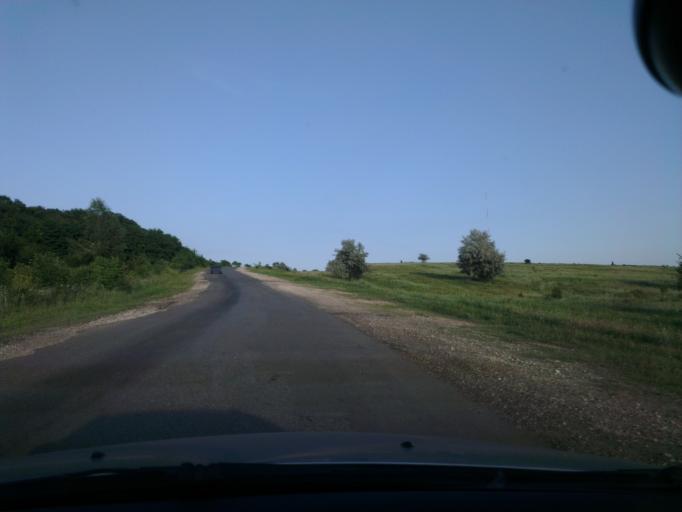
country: MD
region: Cantemir
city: Visniovca
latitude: 46.3658
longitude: 28.3898
